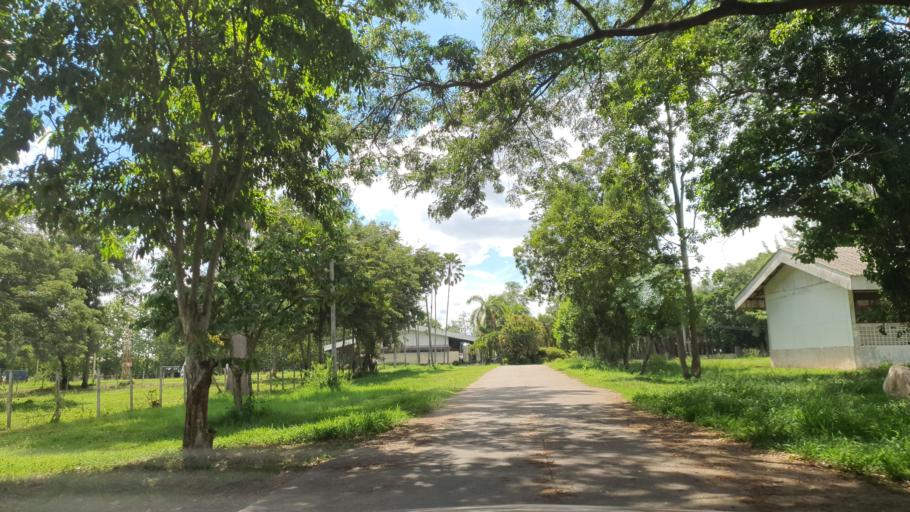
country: TH
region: Chiang Mai
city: San Pa Tong
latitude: 18.5799
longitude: 98.8752
